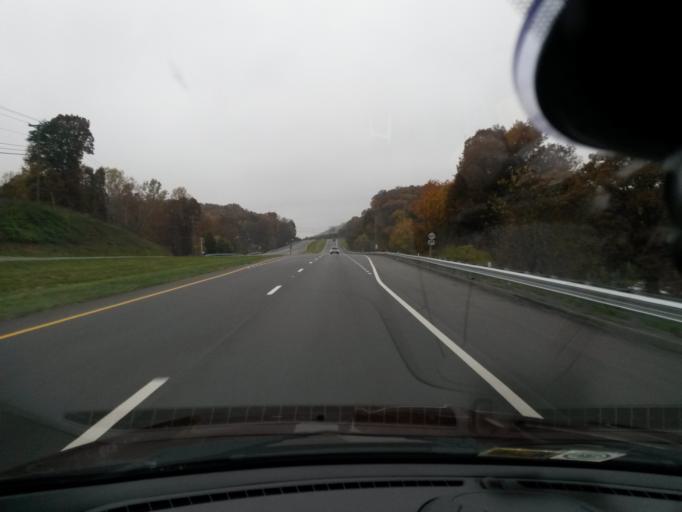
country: US
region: Virginia
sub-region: Botetourt County
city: Cloverdale
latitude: 37.3684
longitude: -79.8866
